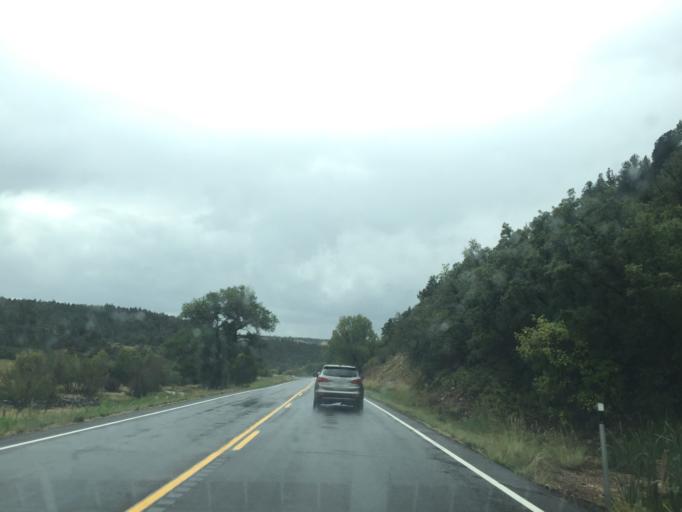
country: US
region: Utah
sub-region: Kane County
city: Kanab
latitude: 37.3387
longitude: -112.6049
